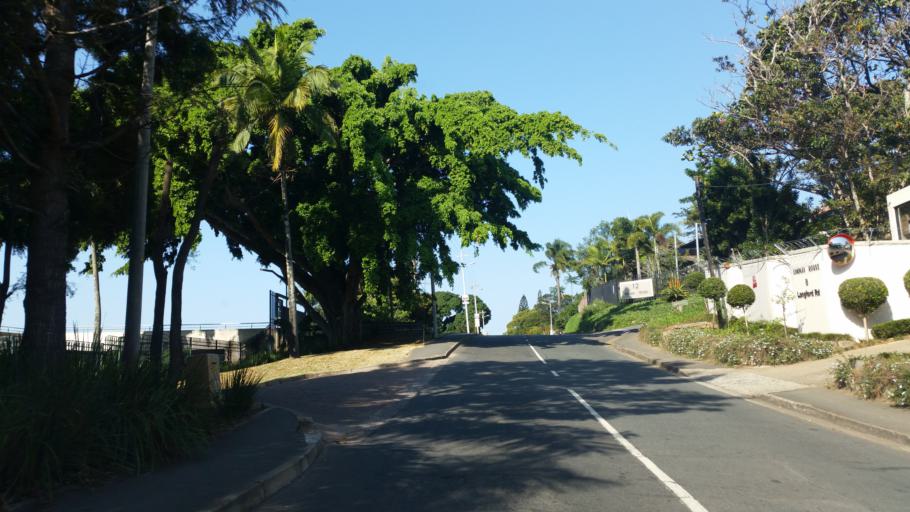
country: ZA
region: KwaZulu-Natal
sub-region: eThekwini Metropolitan Municipality
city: Berea
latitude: -29.8355
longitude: 30.9129
